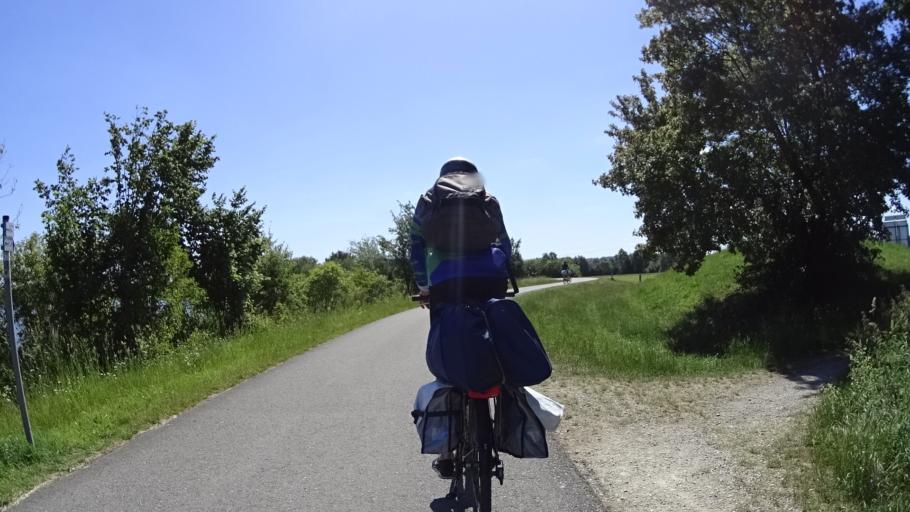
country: DE
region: Bavaria
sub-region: Regierungsbezirk Mittelfranken
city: Gunzenhausen
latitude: 49.1234
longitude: 10.7432
